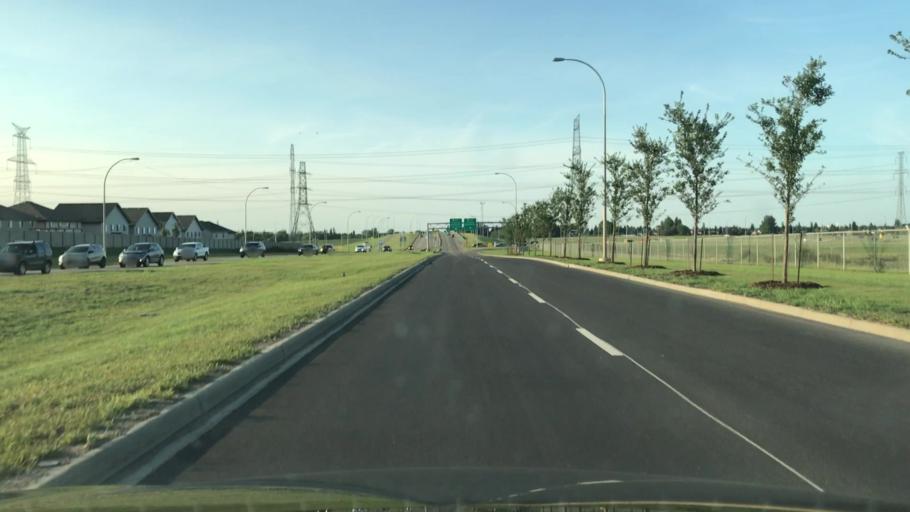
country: CA
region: Alberta
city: Beaumont
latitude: 53.4298
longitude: -113.4178
